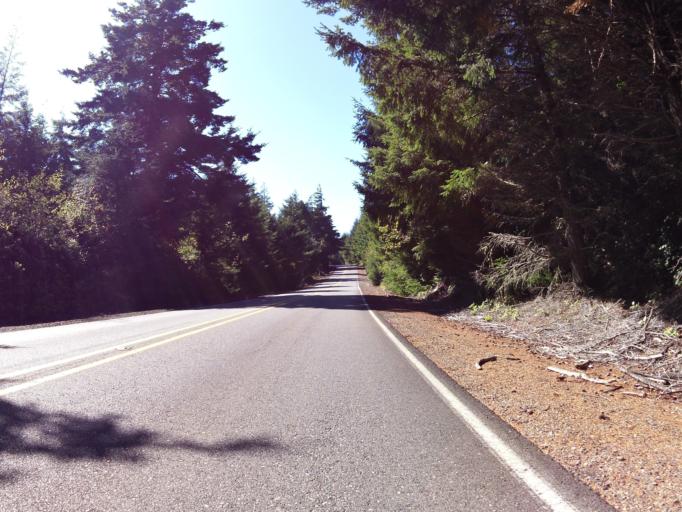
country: US
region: Oregon
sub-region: Coos County
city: Barview
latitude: 43.2419
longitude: -124.3344
